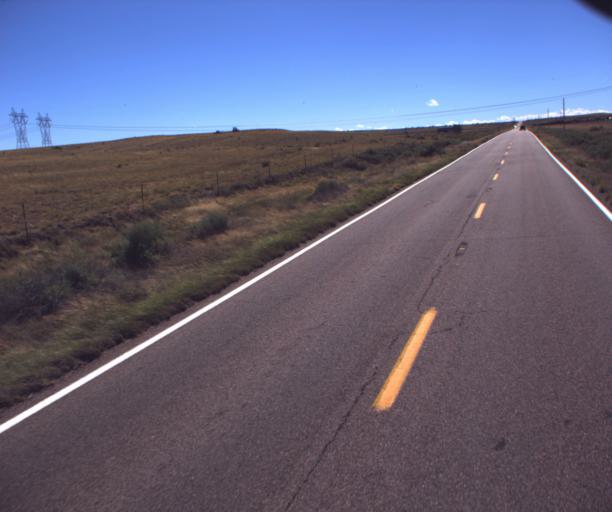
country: US
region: Arizona
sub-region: Apache County
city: Saint Johns
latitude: 34.5809
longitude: -109.3331
